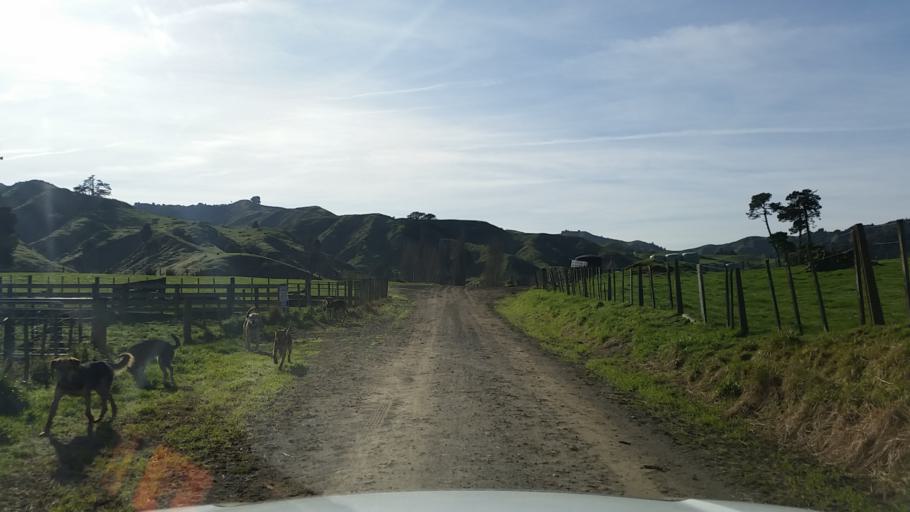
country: NZ
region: Taranaki
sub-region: South Taranaki District
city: Eltham
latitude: -39.3111
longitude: 174.5402
